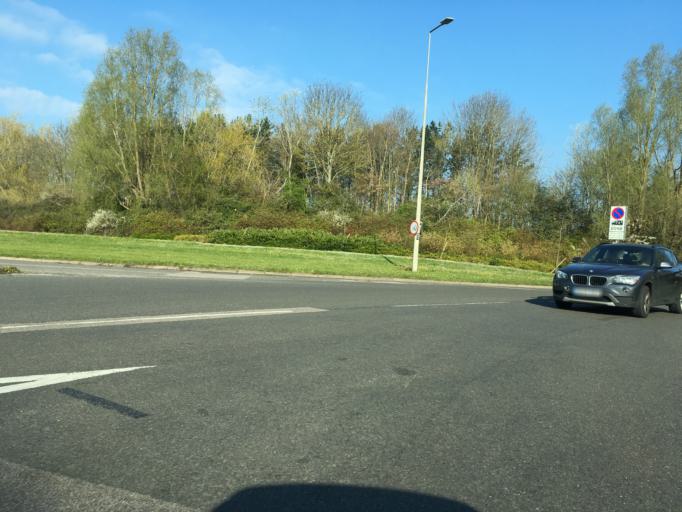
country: GB
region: England
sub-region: Milton Keynes
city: Newport Pagnell
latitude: 52.0652
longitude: -0.7272
